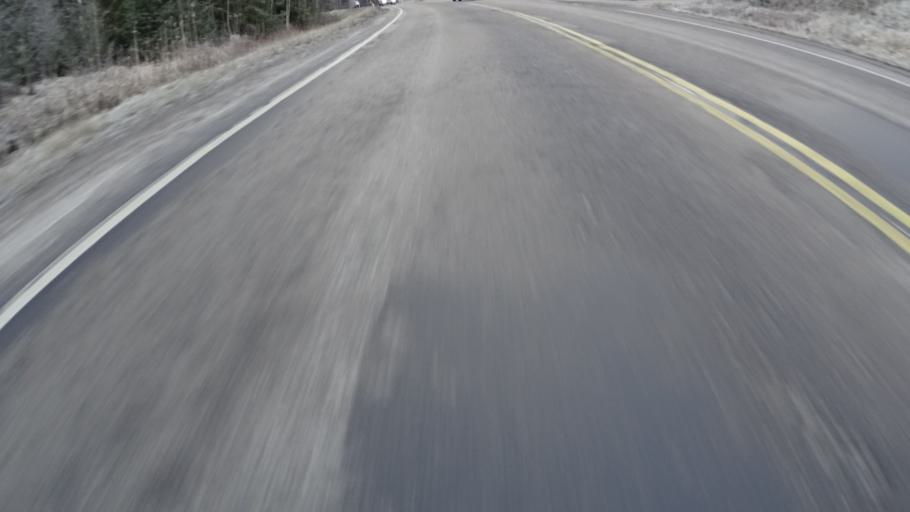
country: FI
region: Uusimaa
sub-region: Helsinki
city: Nurmijaervi
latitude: 60.4206
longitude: 24.7312
